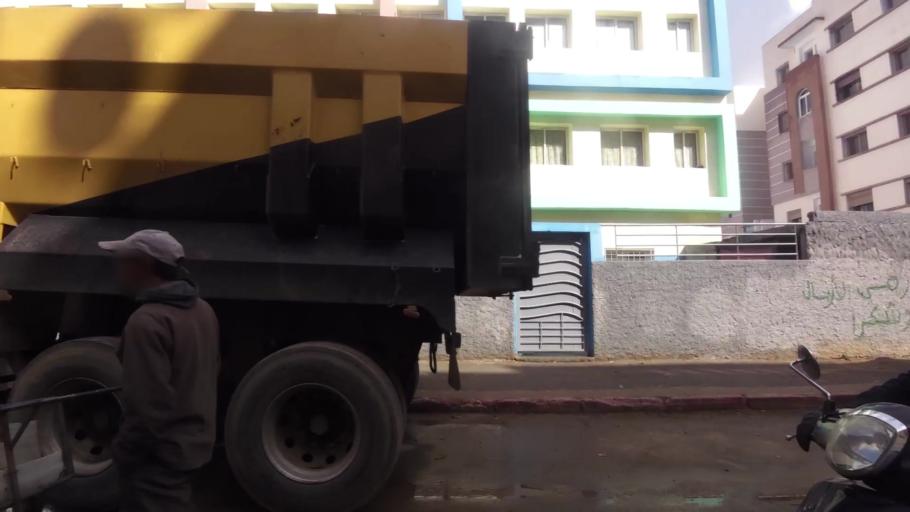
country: MA
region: Grand Casablanca
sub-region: Nouaceur
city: Bouskoura
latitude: 33.5312
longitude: -7.6862
